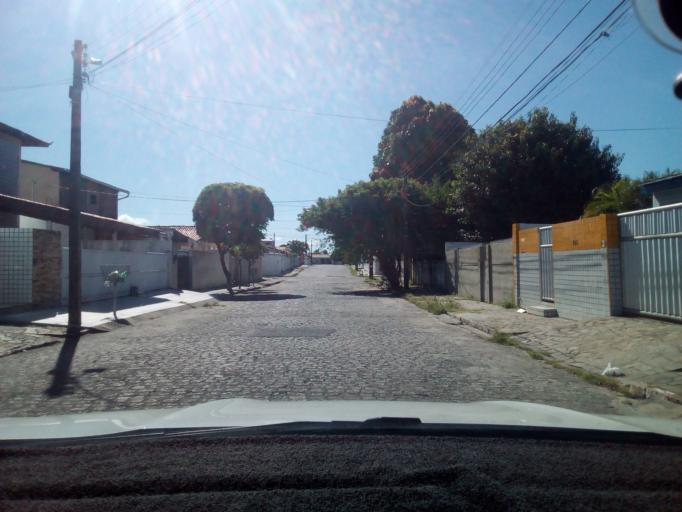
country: BR
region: Paraiba
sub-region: Joao Pessoa
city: Joao Pessoa
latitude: -7.1135
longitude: -34.8629
